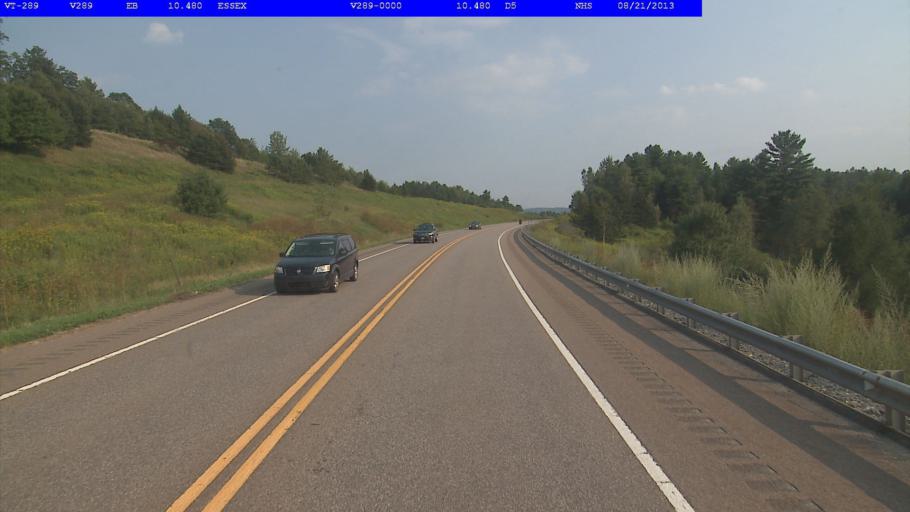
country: US
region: Vermont
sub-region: Chittenden County
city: Essex Junction
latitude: 44.5000
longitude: -73.0710
